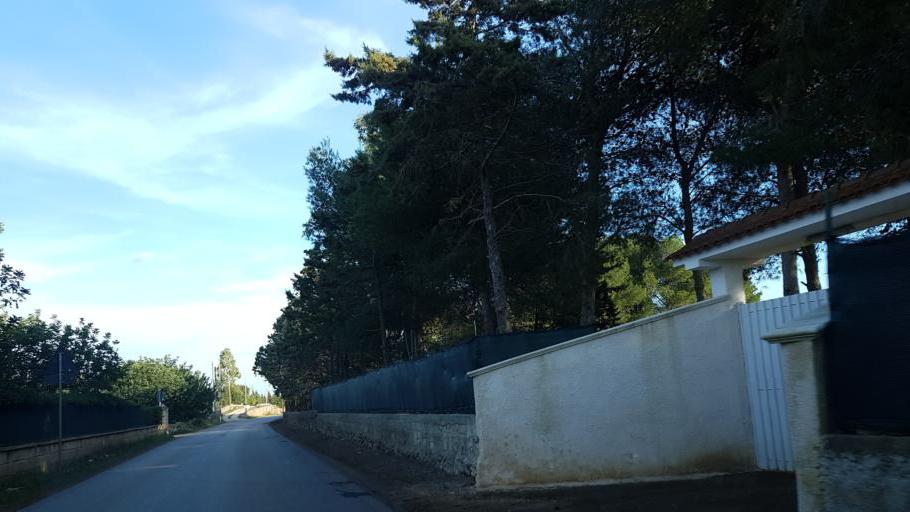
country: IT
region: Apulia
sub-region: Provincia di Brindisi
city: San Vito dei Normanni
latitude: 40.7047
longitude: 17.7132
